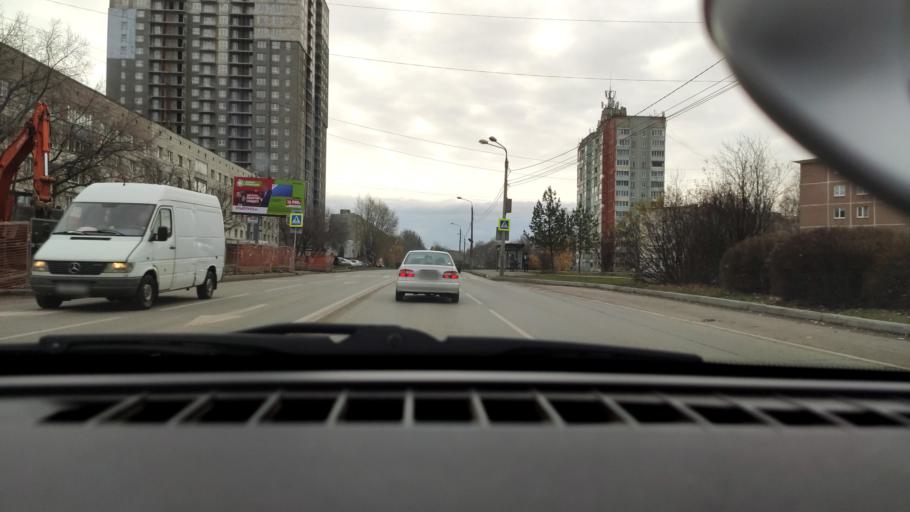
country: RU
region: Perm
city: Kondratovo
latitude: 57.9682
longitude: 56.1741
